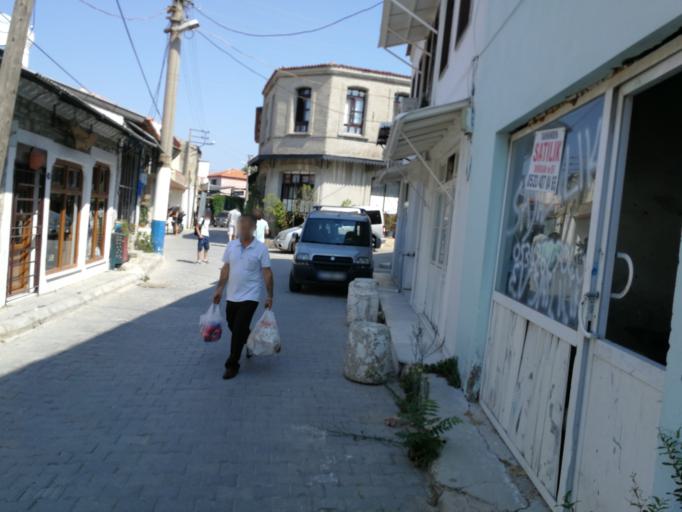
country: TR
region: Izmir
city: Urla
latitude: 38.3216
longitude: 26.7672
